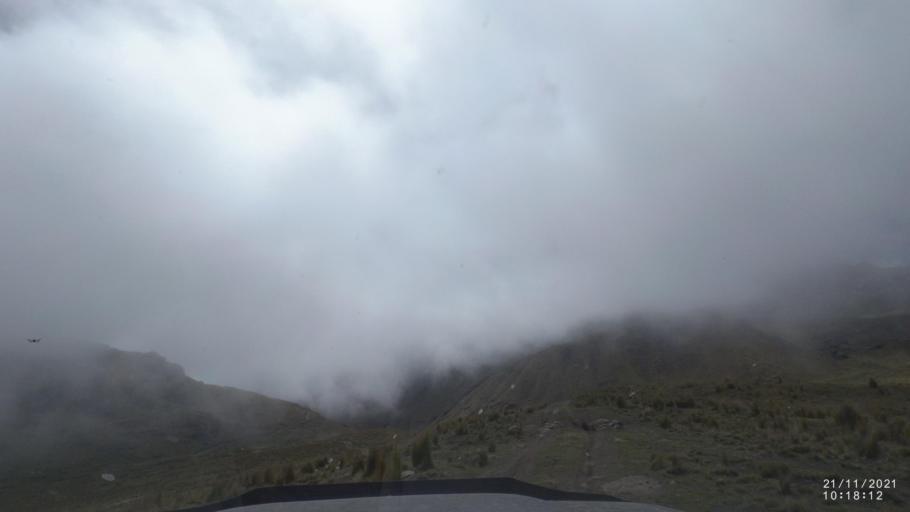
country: BO
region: Cochabamba
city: Cochabamba
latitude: -16.9920
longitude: -66.2674
